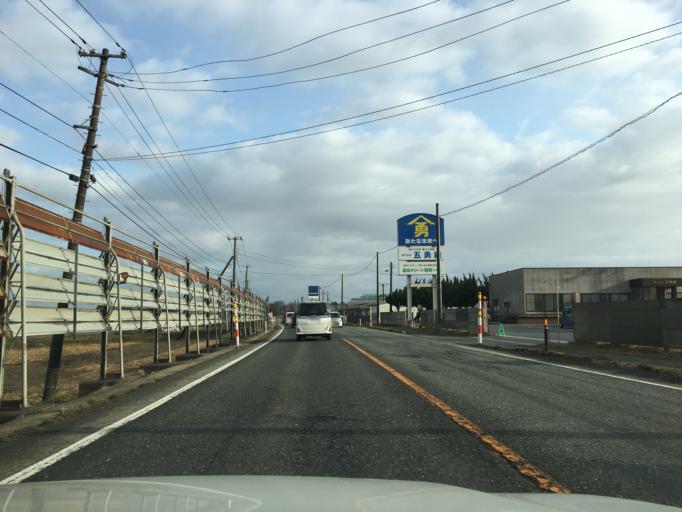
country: JP
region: Yamagata
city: Sakata
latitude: 38.8393
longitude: 139.8487
